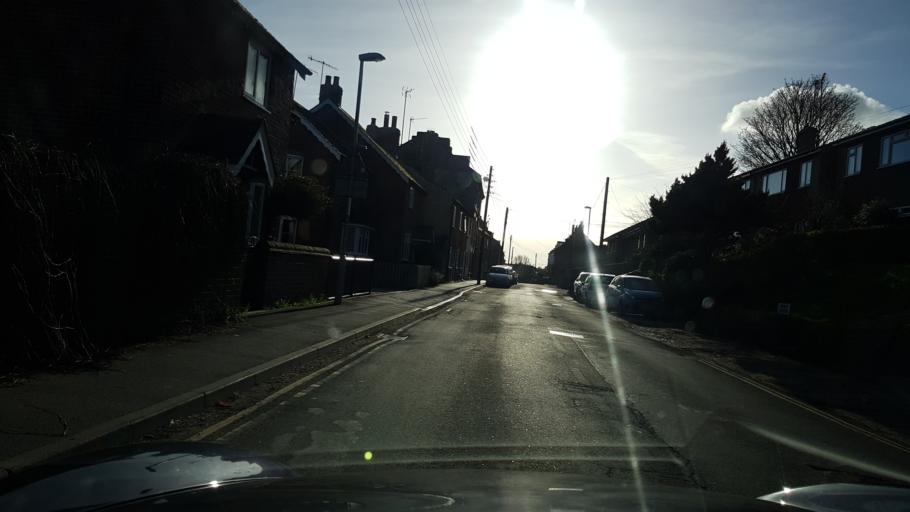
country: GB
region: England
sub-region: Dorset
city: Bridport
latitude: 50.7390
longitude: -2.7649
